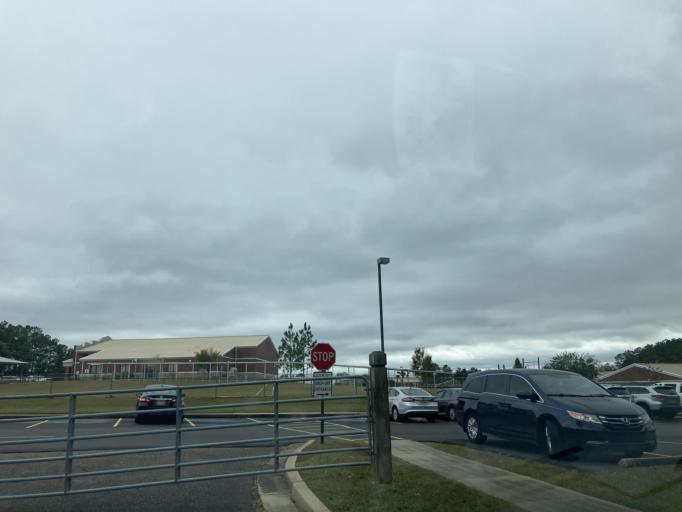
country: US
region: Mississippi
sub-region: Lamar County
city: West Hattiesburg
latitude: 31.2824
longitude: -89.4729
